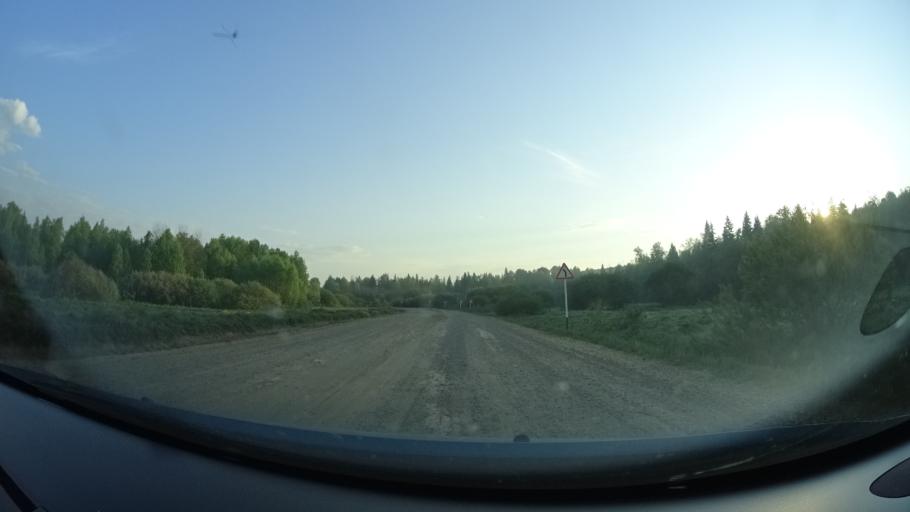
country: RU
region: Perm
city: Kuyeda
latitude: 56.6200
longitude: 55.7105
